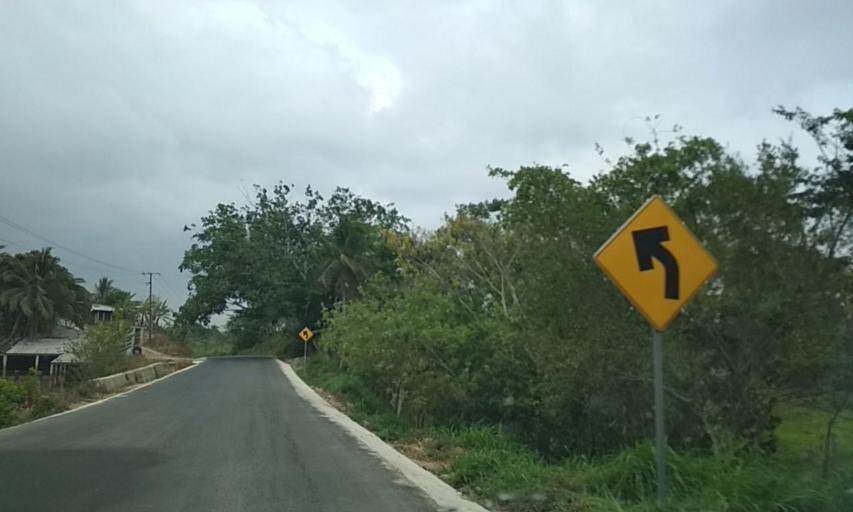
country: MX
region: Tabasco
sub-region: Huimanguillo
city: Francisco Rueda
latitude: 17.7295
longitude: -94.1020
